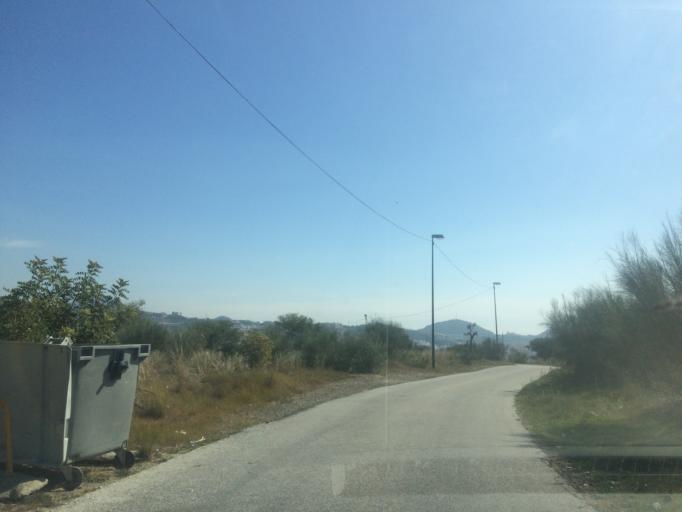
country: ES
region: Andalusia
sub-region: Provincia de Malaga
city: Malaga
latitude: 36.7530
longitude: -4.4375
